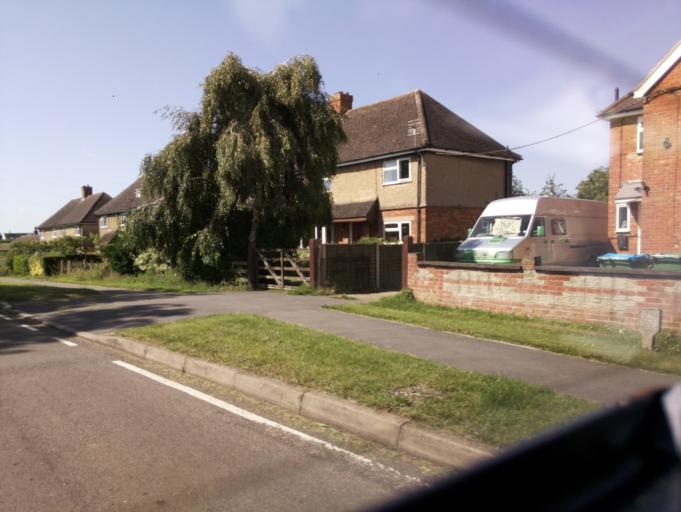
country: GB
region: England
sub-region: Milton Keynes
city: Calverton
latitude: 52.0028
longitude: -0.8660
